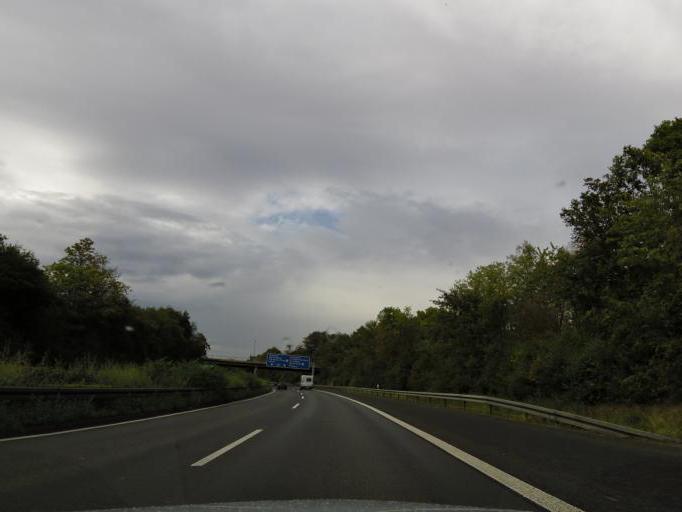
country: DE
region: Hesse
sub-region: Regierungsbezirk Darmstadt
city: Bad Homburg vor der Hoehe
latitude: 50.1871
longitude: 8.6581
